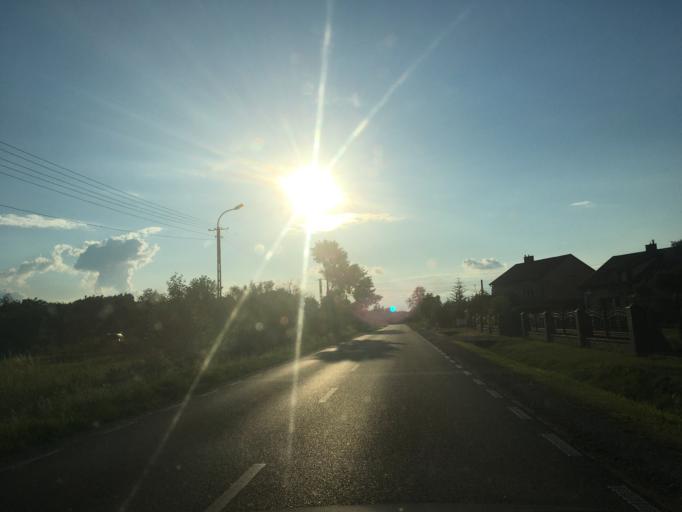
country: PL
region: Masovian Voivodeship
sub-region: Powiat grodziski
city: Grodzisk Mazowiecki
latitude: 52.1187
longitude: 20.5775
